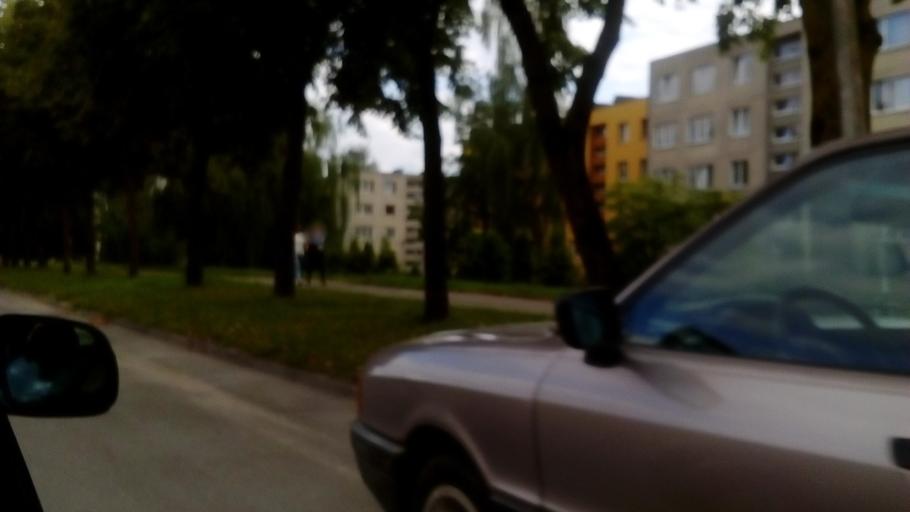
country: LT
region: Alytaus apskritis
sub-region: Alytus
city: Alytus
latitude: 54.4132
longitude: 24.0210
